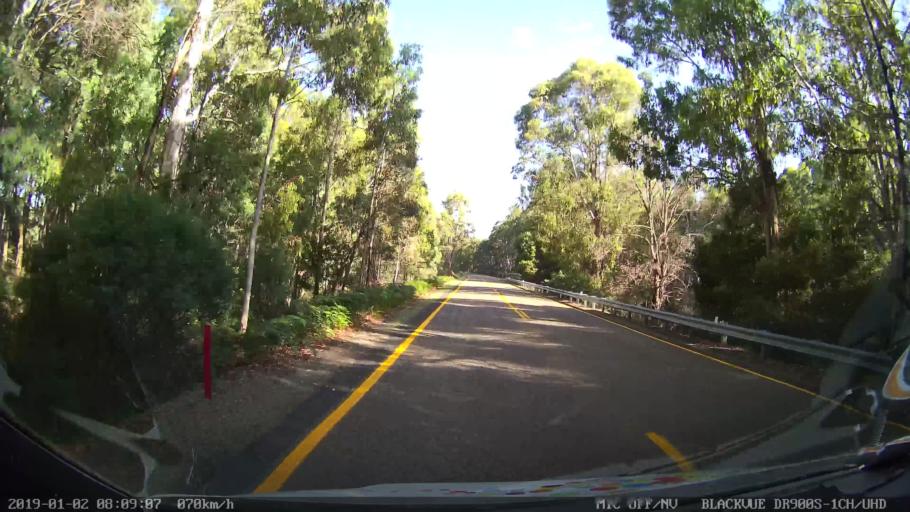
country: AU
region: New South Wales
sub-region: Tumut Shire
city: Tumut
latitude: -35.6101
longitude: 148.3812
